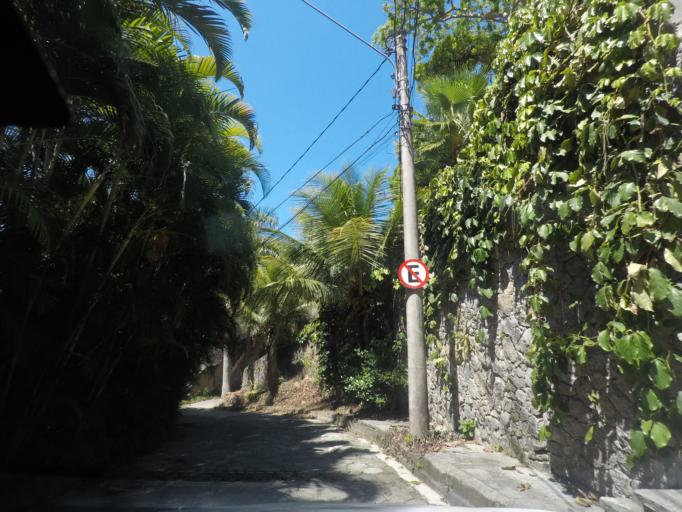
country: BR
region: Rio de Janeiro
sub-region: Niteroi
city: Niteroi
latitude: -22.9706
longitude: -43.0350
